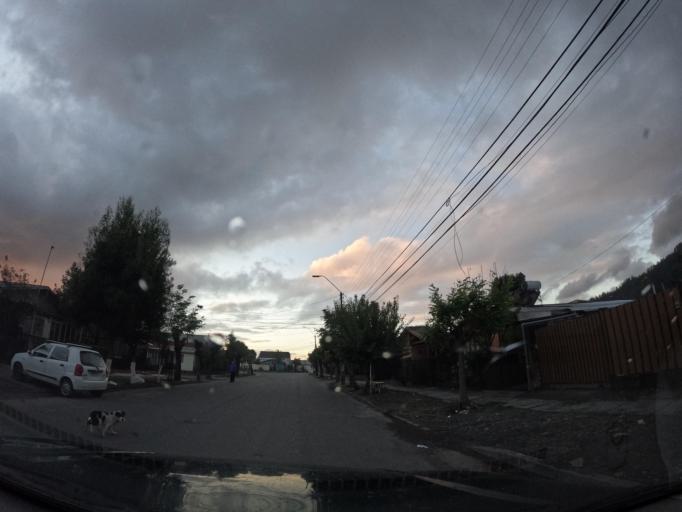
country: CL
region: Biobio
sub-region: Provincia de Concepcion
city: Chiguayante
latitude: -36.9270
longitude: -73.0275
